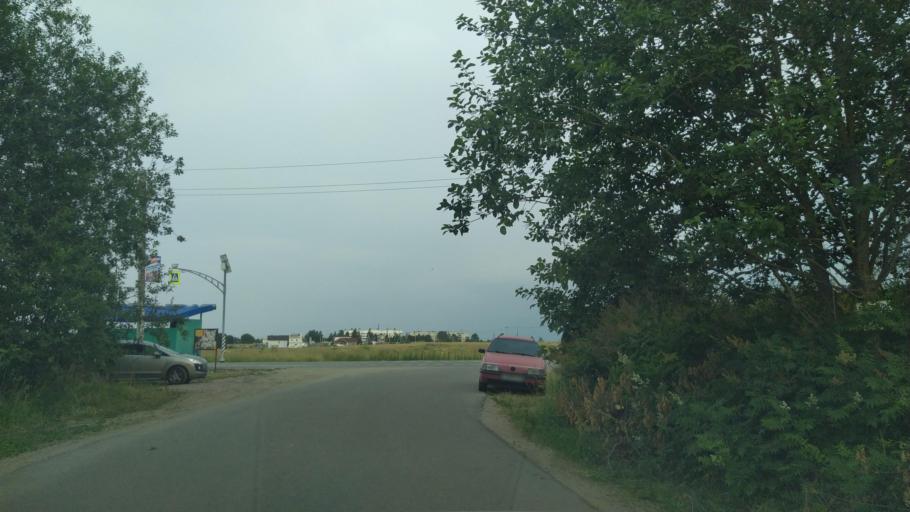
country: RU
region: Leningrad
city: Koltushi
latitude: 59.8906
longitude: 30.7329
